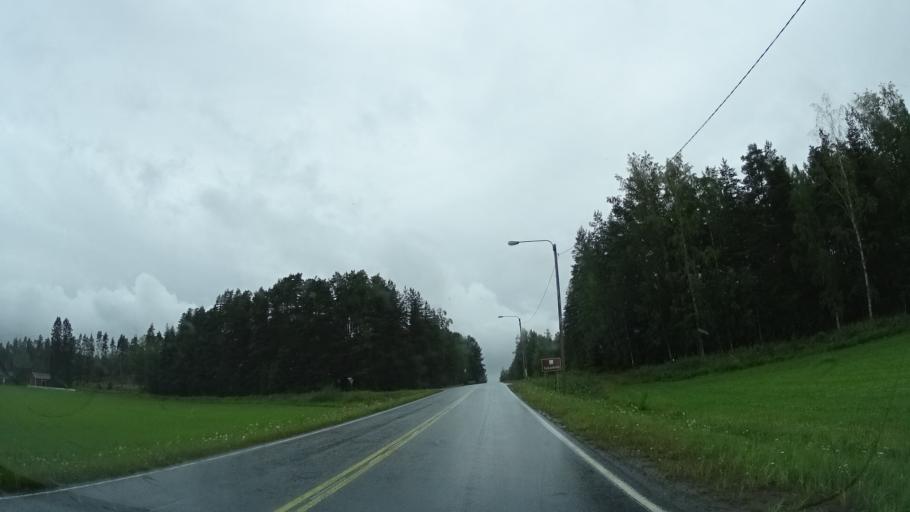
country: FI
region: Haeme
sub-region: Forssa
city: Humppila
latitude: 60.9741
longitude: 23.2524
